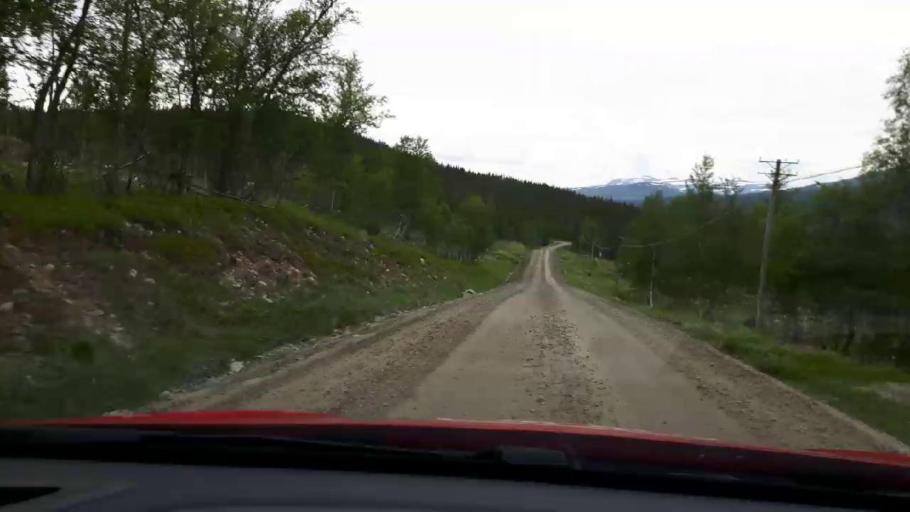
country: SE
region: Jaemtland
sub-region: Are Kommun
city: Are
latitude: 62.8448
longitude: 12.7922
